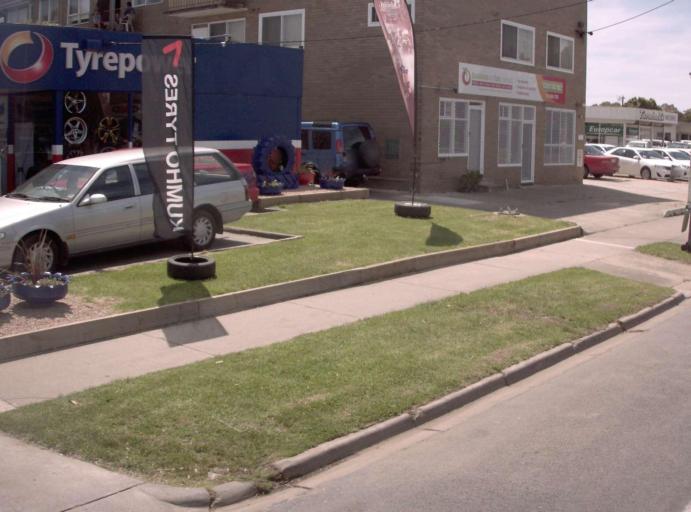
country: AU
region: Victoria
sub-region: Wellington
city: Sale
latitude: -38.1024
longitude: 147.0679
